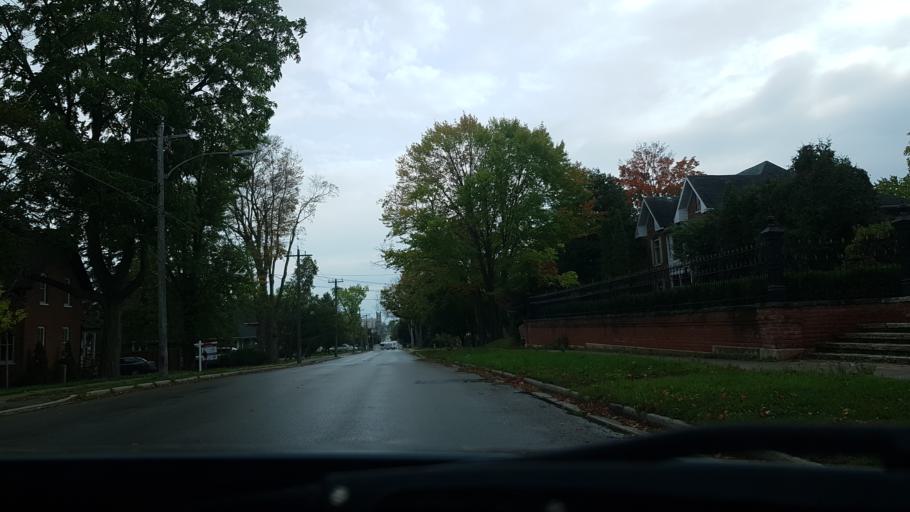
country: CA
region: Ontario
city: Omemee
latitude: 44.3630
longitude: -78.7408
